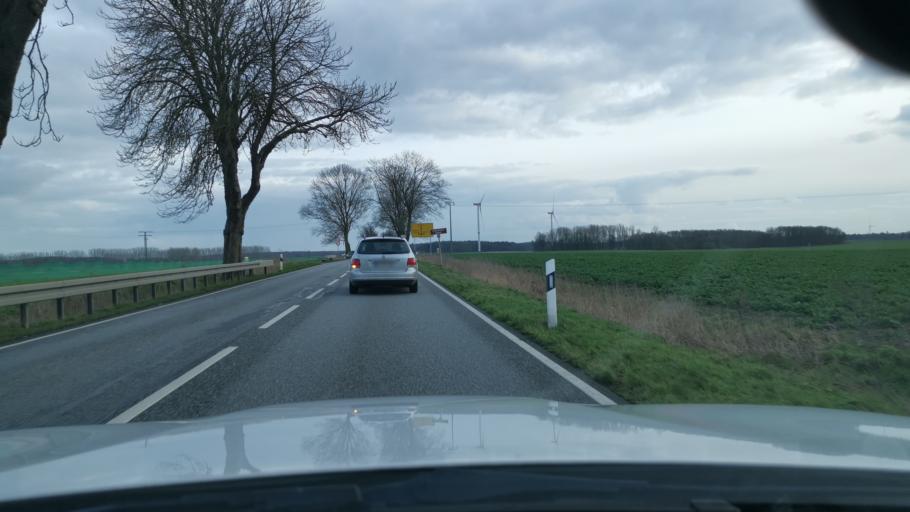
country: DE
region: Mecklenburg-Vorpommern
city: Dummerstorf
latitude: 54.0184
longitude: 12.2453
